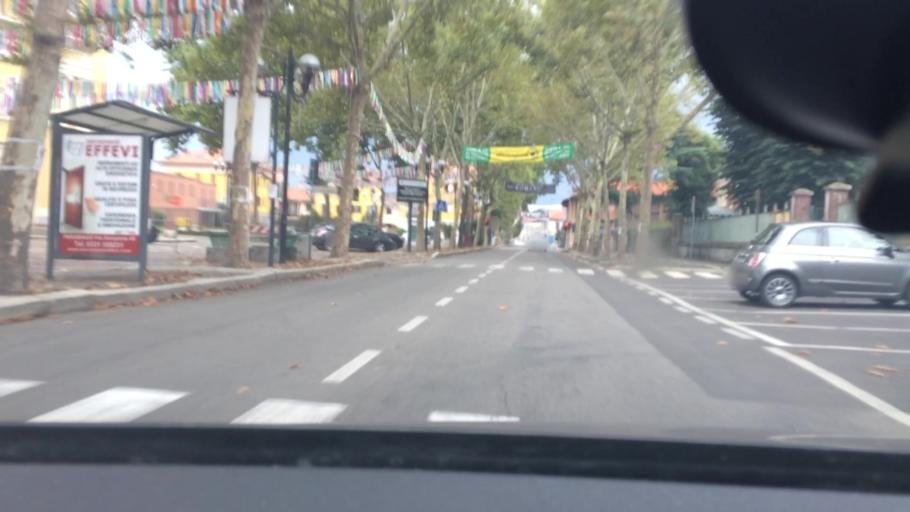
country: IT
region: Lombardy
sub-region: Citta metropolitana di Milano
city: Cantalupo
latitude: 45.5789
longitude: 8.9793
